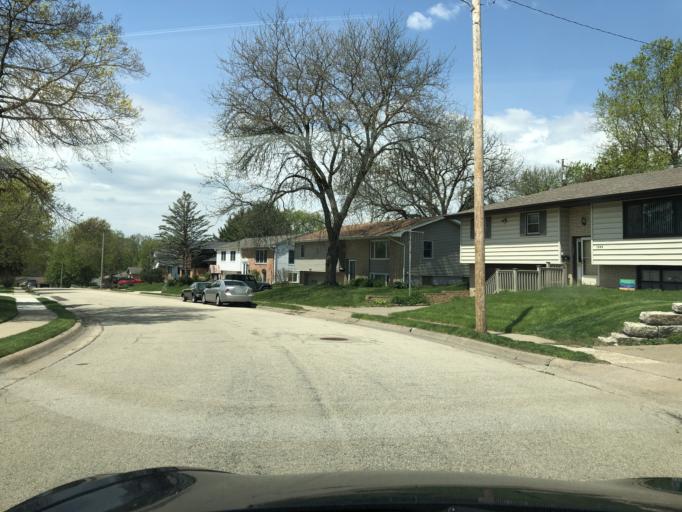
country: US
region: Iowa
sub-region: Dubuque County
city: Dubuque
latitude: 42.4750
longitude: -90.6705
